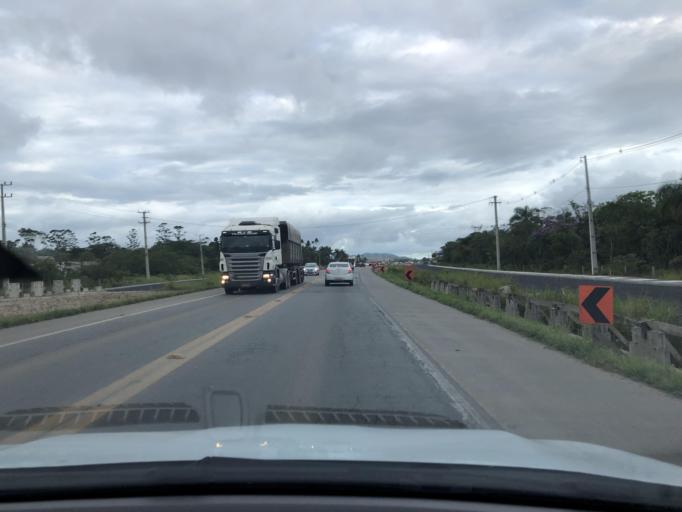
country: BR
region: Santa Catarina
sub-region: Joinville
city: Joinville
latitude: -26.3928
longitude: -48.7373
